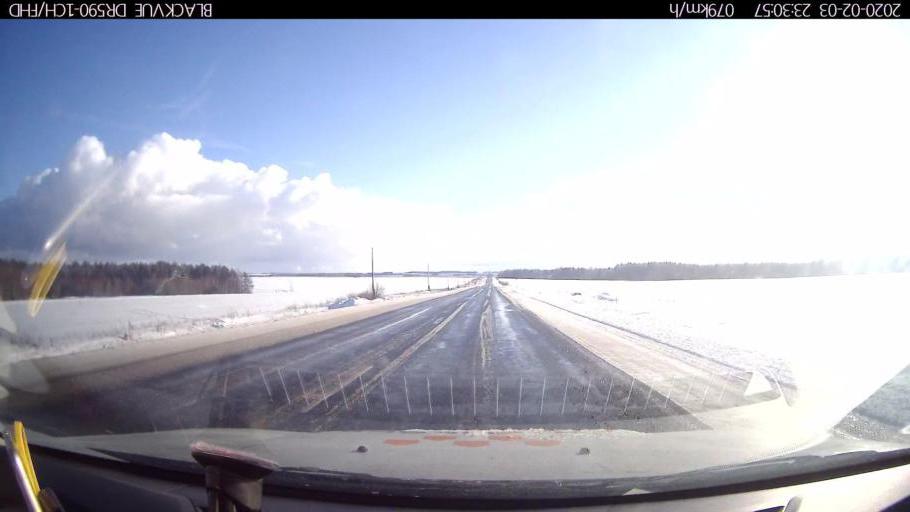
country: RU
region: Nizjnij Novgorod
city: Dal'neye Konstantinovo
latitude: 55.9474
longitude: 44.2205
